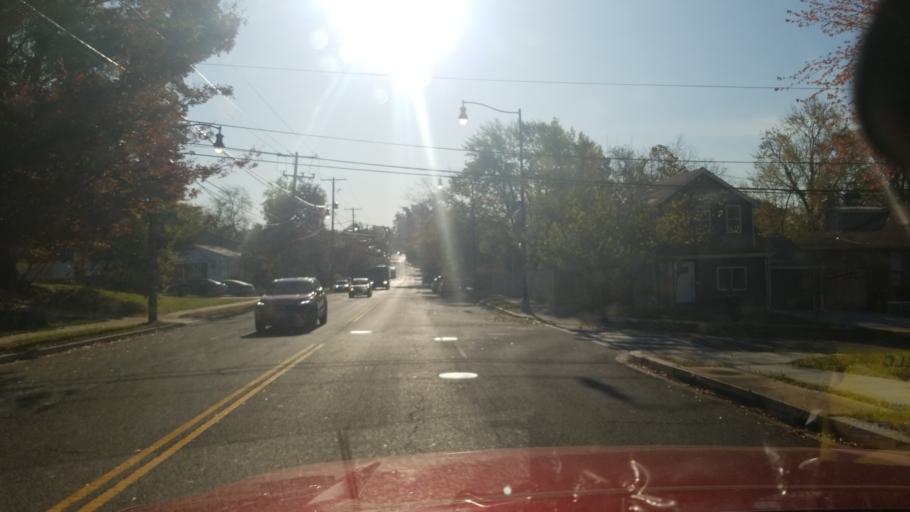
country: US
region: Maryland
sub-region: Prince George's County
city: Fairmount Heights
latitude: 38.9013
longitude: -76.9202
